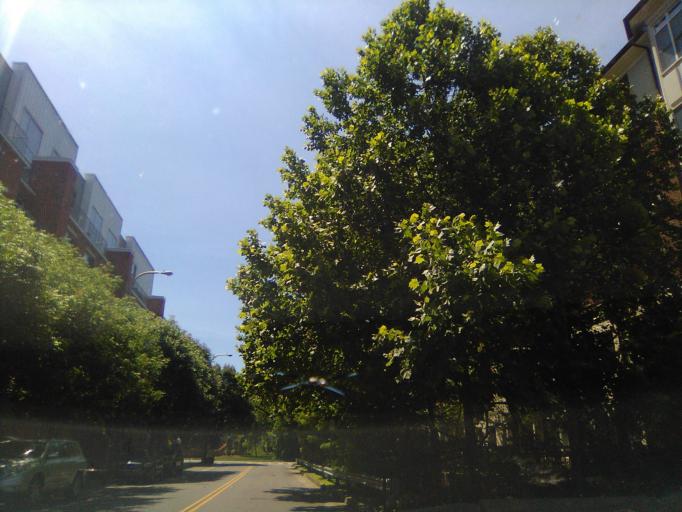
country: US
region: Tennessee
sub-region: Davidson County
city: Belle Meade
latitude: 36.1255
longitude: -86.8447
